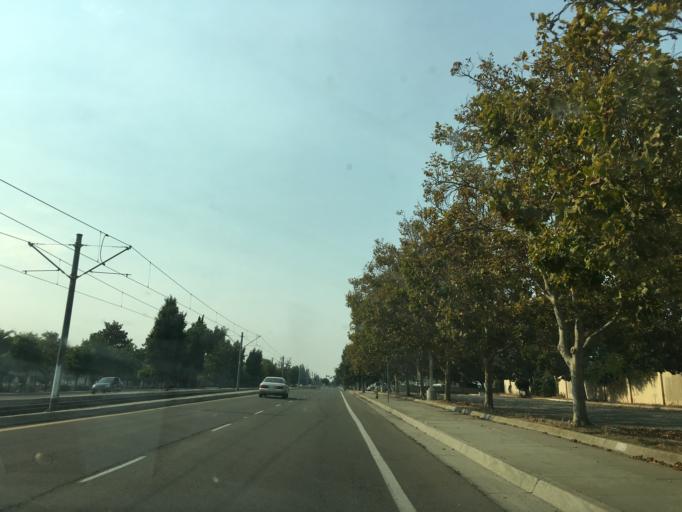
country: US
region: California
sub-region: Santa Clara County
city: Alum Rock
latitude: 37.3632
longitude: -121.8360
